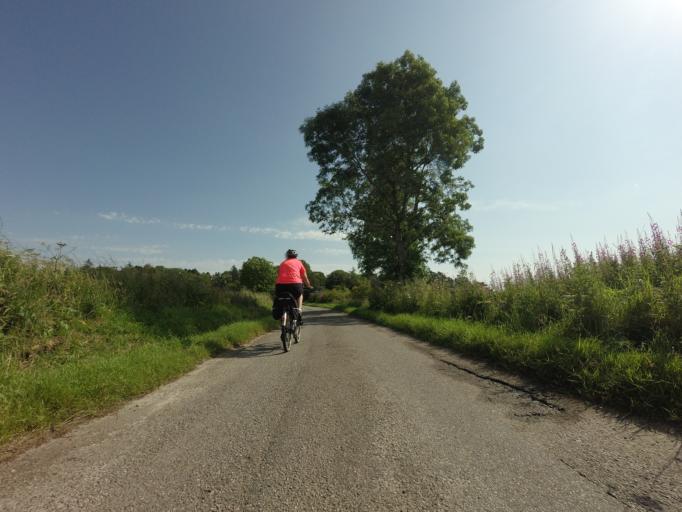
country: GB
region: Scotland
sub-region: Highland
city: Alness
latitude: 57.7142
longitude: -4.2189
